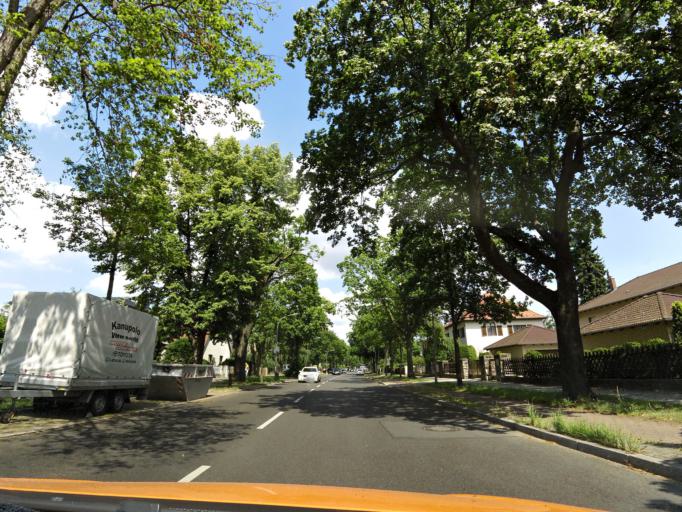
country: DE
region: Berlin
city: Wilhelmstadt
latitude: 52.5117
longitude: 13.1723
